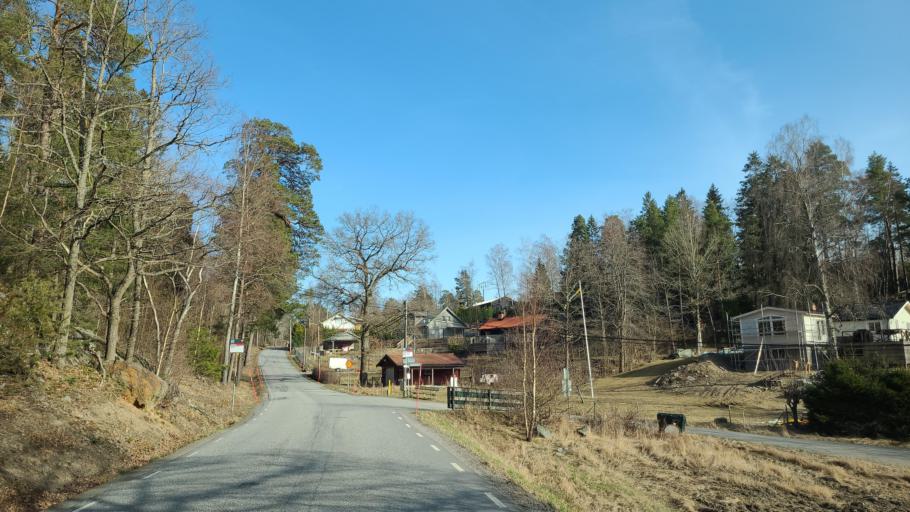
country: SE
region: Stockholm
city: Stenhamra
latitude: 59.2781
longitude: 17.6795
